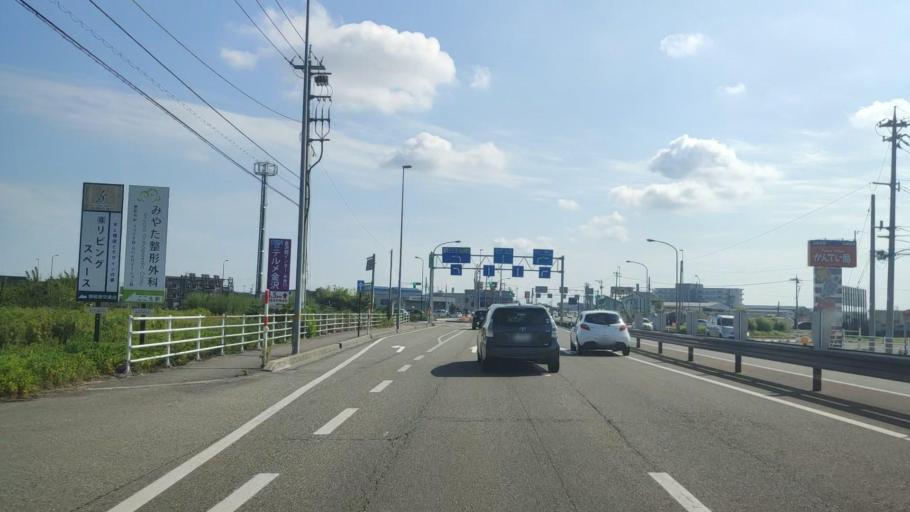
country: JP
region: Ishikawa
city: Matsuto
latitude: 36.5236
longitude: 136.5824
